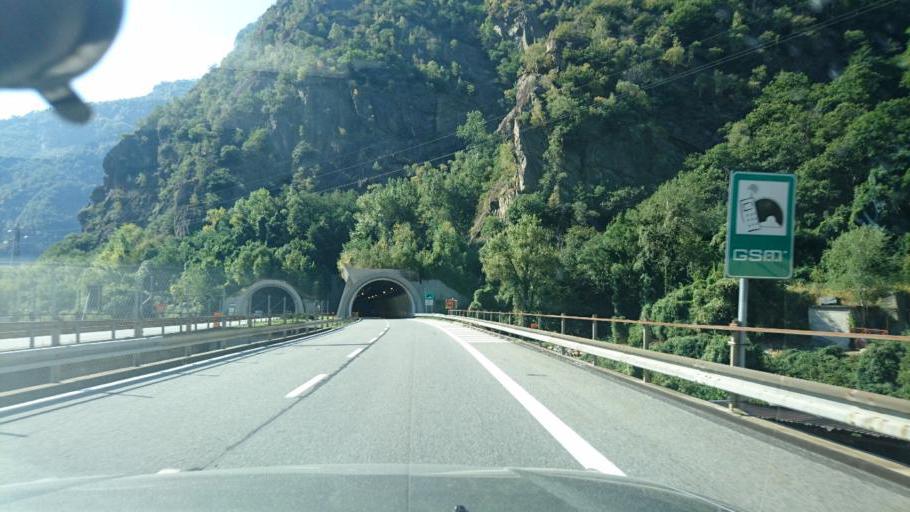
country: IT
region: Aosta Valley
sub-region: Valle d'Aosta
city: Hone
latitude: 45.6101
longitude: 7.7385
